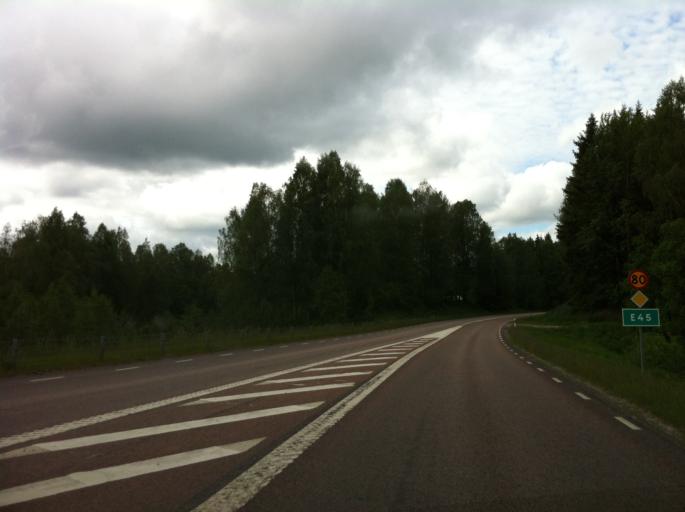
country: SE
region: Vaermland
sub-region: Sunne Kommun
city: Sunne
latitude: 59.8077
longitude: 13.1250
